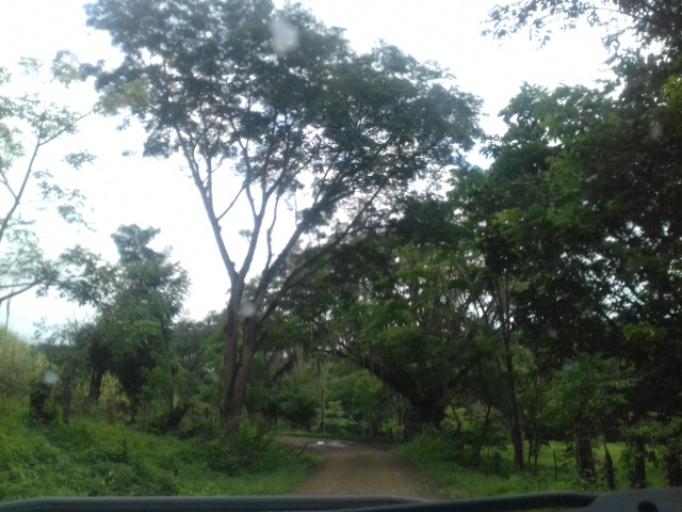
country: NI
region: Matagalpa
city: Matiguas
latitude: 12.8616
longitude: -85.3891
